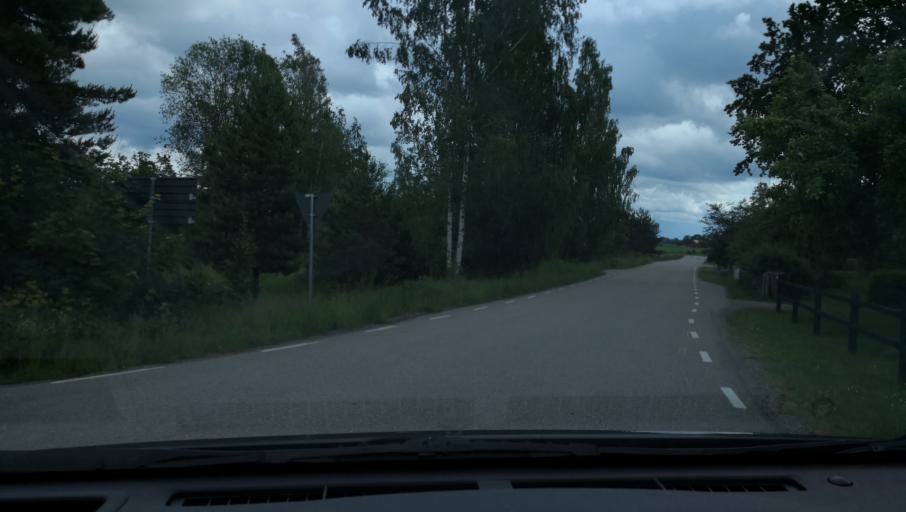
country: SE
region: OErebro
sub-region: Lindesbergs Kommun
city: Fellingsbro
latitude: 59.3267
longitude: 15.6769
